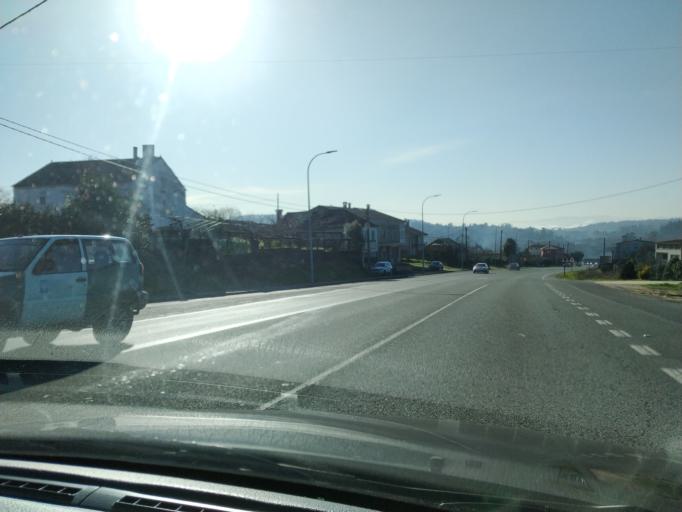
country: ES
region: Galicia
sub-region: Provincia da Coruna
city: Santiago de Compostela
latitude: 42.8484
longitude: -8.5252
